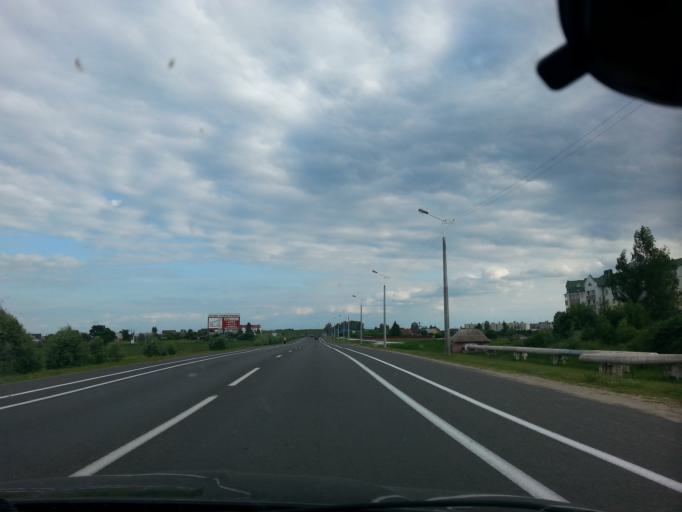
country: BY
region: Minsk
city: Myadzyel
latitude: 54.8821
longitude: 26.9390
